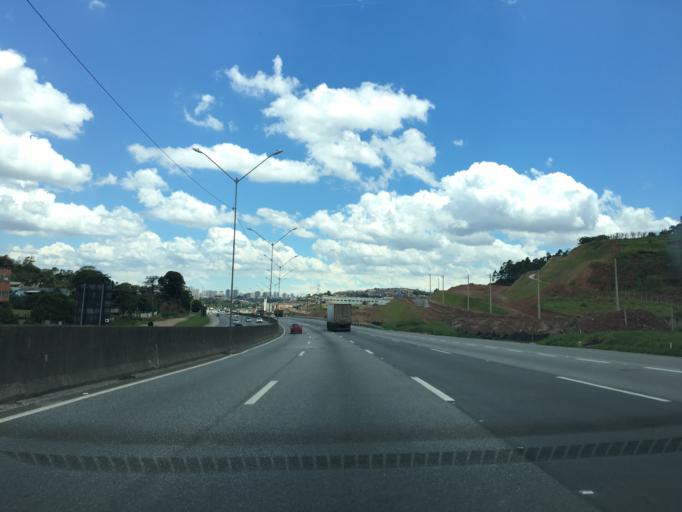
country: BR
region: Sao Paulo
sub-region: Guarulhos
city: Guarulhos
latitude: -23.4196
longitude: -46.5789
